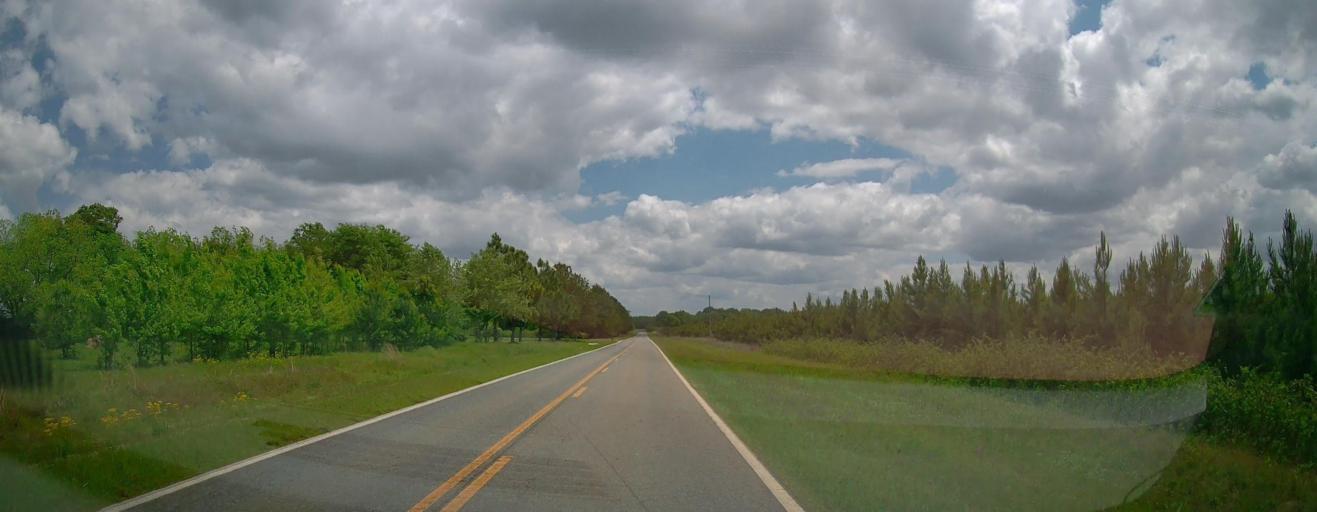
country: US
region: Georgia
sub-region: Laurens County
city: Dublin
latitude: 32.6027
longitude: -82.9865
